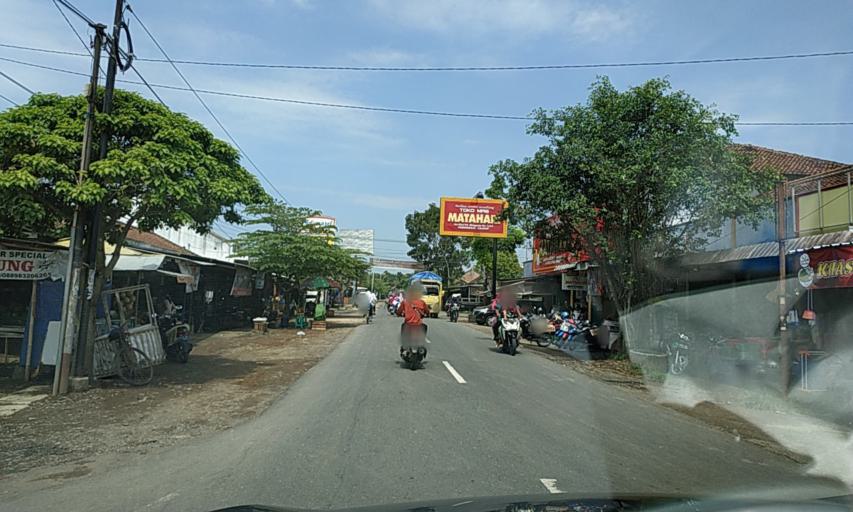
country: ID
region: Central Java
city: Mulyosari
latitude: -7.5078
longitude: 108.7852
